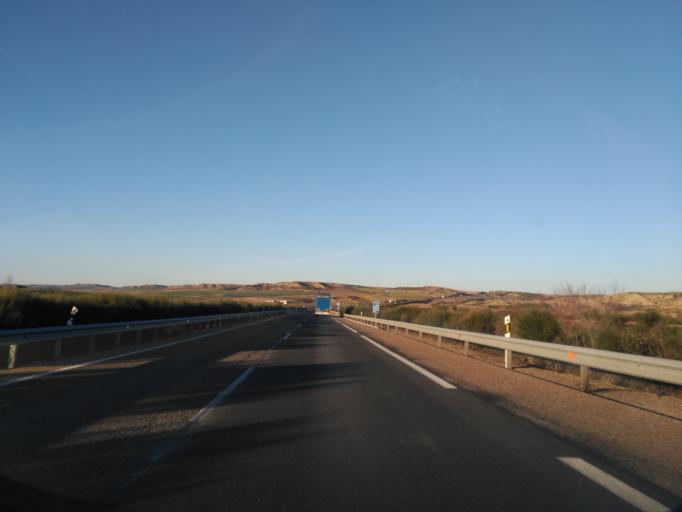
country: ES
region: Castille and Leon
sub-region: Provincia de Zamora
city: Castrillo de la Guarena
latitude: 41.2177
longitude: -5.3198
